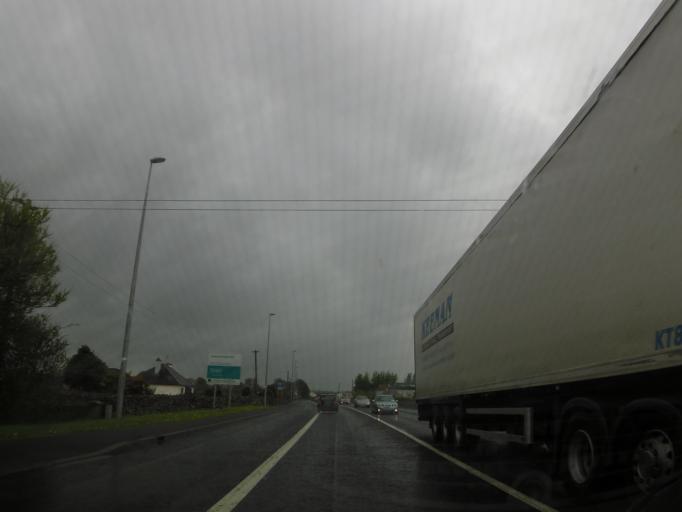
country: IE
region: Connaught
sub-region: County Galway
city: Claregalway
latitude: 53.3512
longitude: -8.9376
